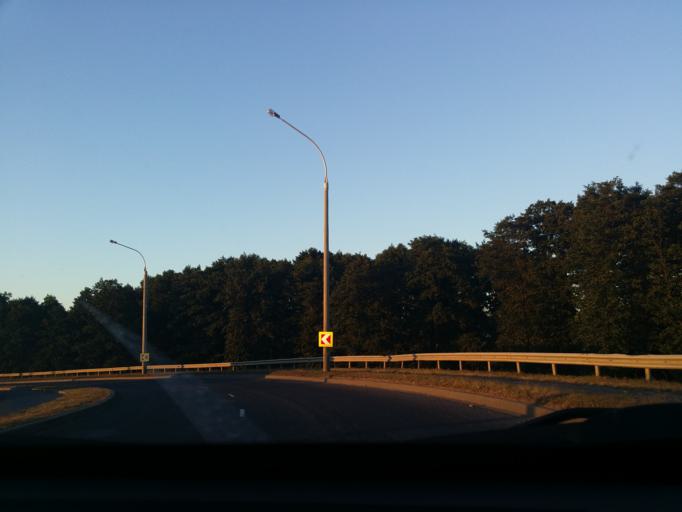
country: BY
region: Minsk
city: Vyaliki Trastsyanets
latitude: 53.8466
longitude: 27.7105
